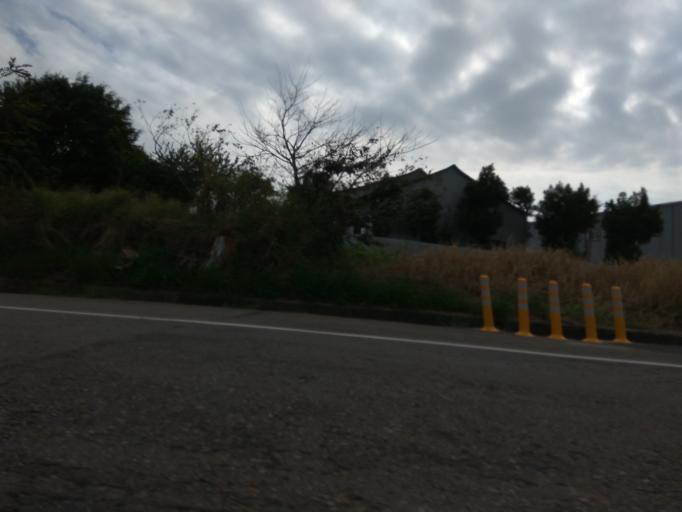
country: TW
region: Taiwan
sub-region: Hsinchu
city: Zhubei
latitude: 24.9688
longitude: 121.0205
